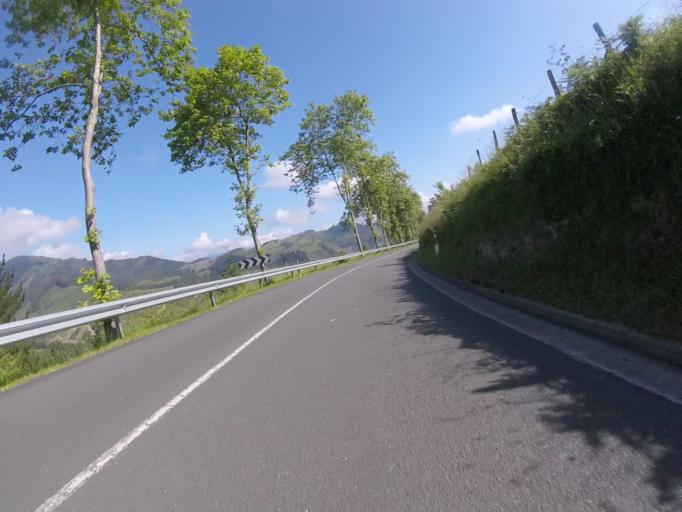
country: ES
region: Basque Country
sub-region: Provincia de Guipuzcoa
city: Ormaiztegui
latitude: 43.0895
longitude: -2.2436
